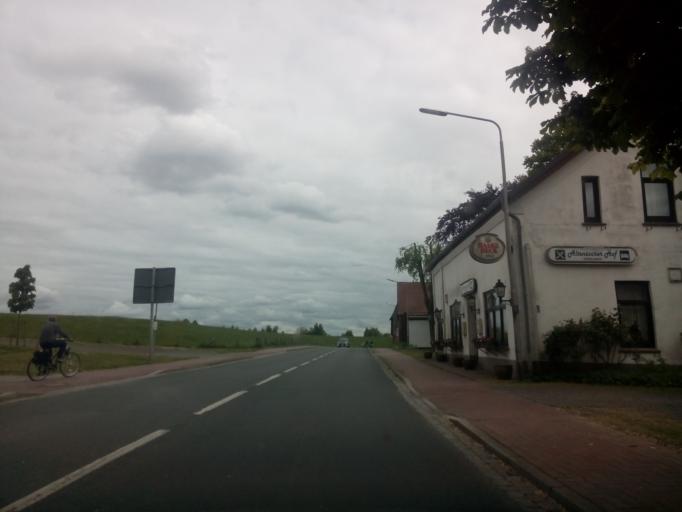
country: DE
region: Lower Saxony
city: Lemwerder
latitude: 53.1335
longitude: 8.6241
